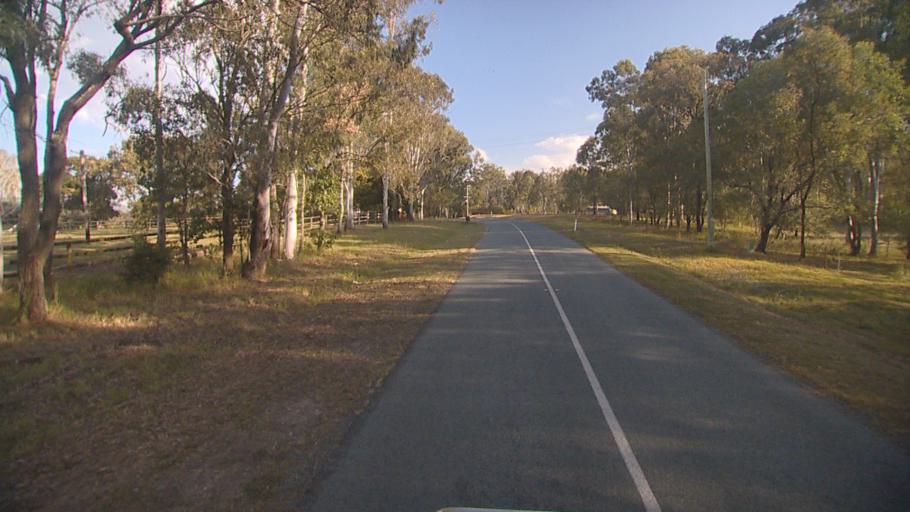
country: AU
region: Queensland
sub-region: Gold Coast
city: Ormeau Hills
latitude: -27.8313
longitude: 153.1707
